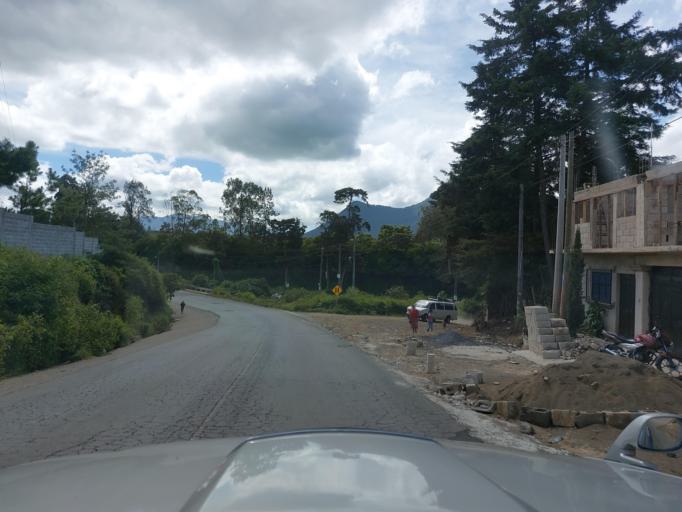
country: GT
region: Chimaltenango
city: Parramos
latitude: 14.6085
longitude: -90.8096
